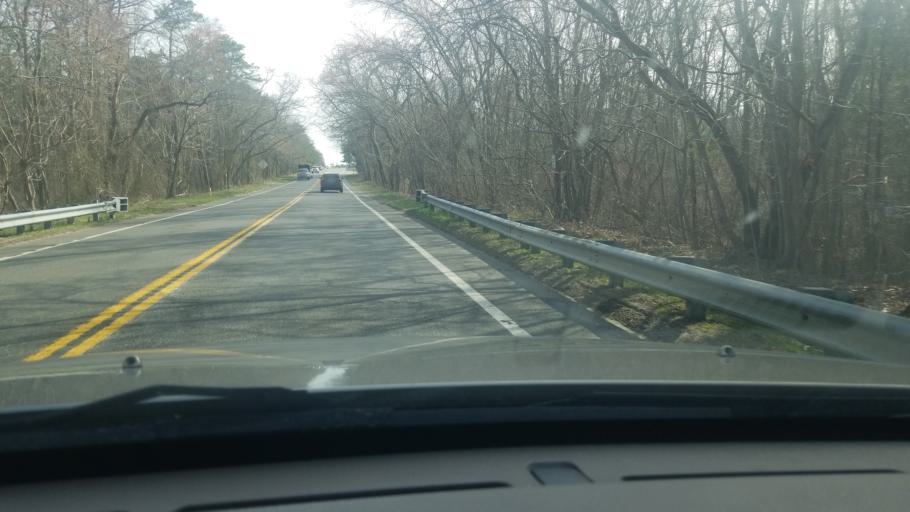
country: US
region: New Jersey
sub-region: Ocean County
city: Cedar Glen West
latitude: 40.0323
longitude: -74.3066
